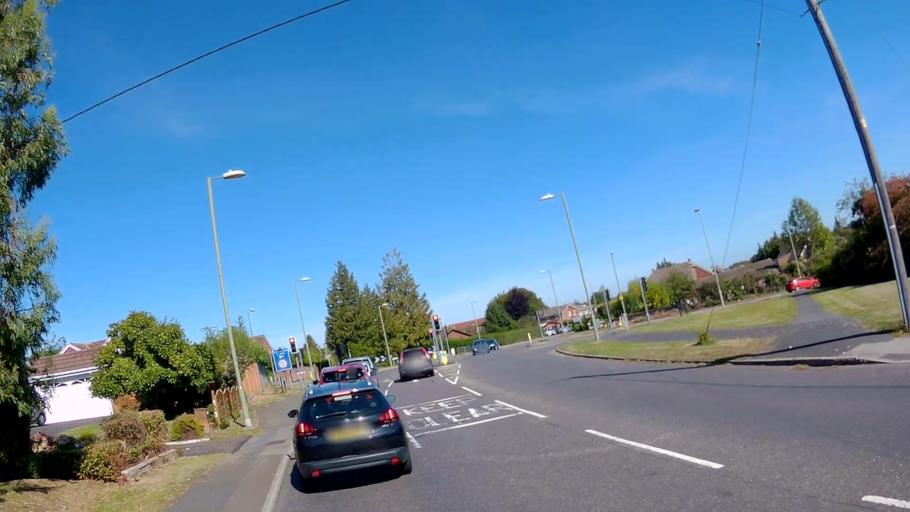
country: GB
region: England
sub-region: Hampshire
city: Basingstoke
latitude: 51.2522
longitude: -1.1386
